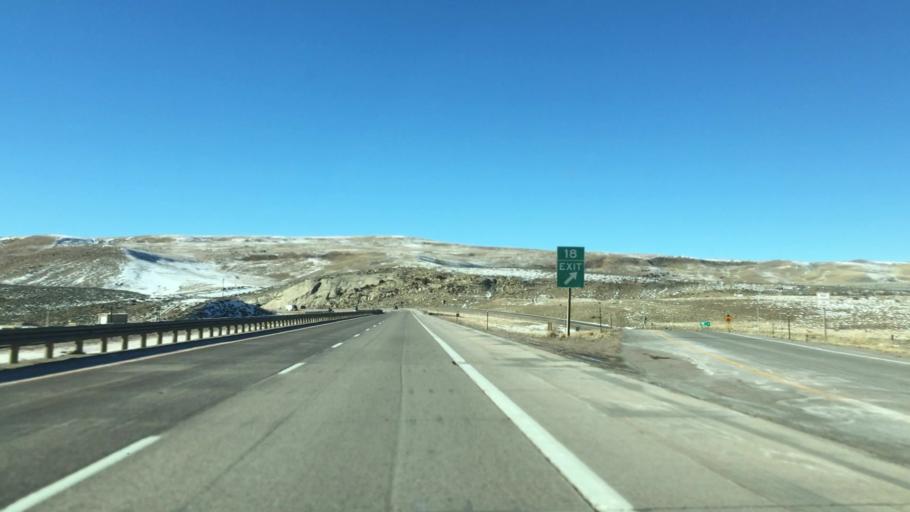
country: US
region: Wyoming
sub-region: Uinta County
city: Evanston
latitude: 41.3073
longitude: -110.7282
